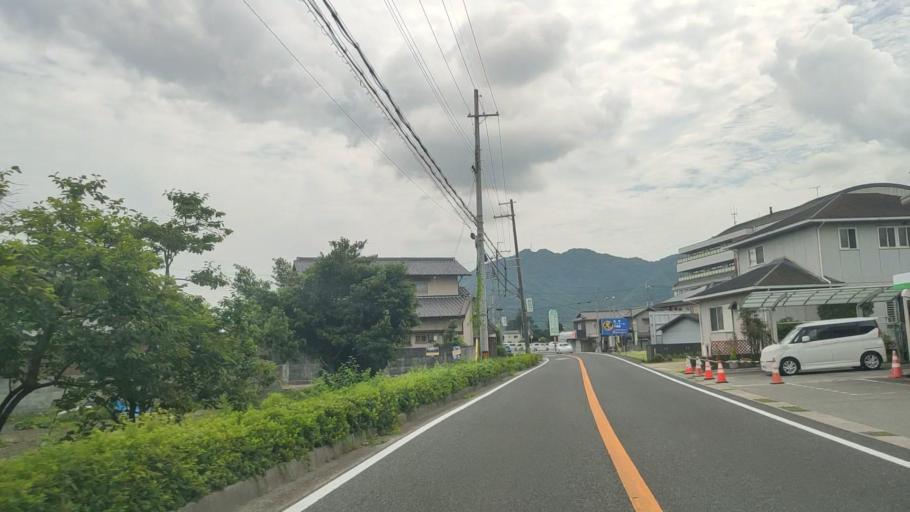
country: JP
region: Hyogo
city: Tatsunocho-tominaga
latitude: 34.9060
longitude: 134.5489
